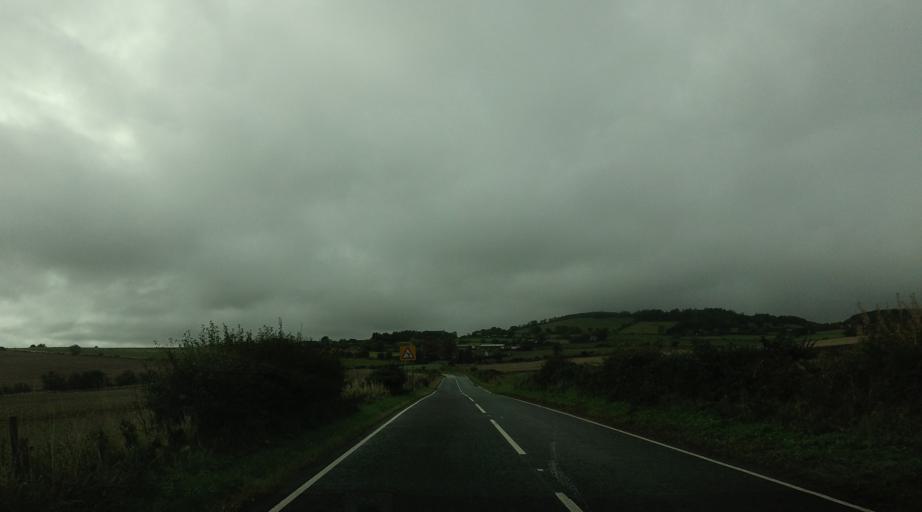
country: GB
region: Scotland
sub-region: Fife
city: Balmullo
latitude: 56.3854
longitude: -2.9195
